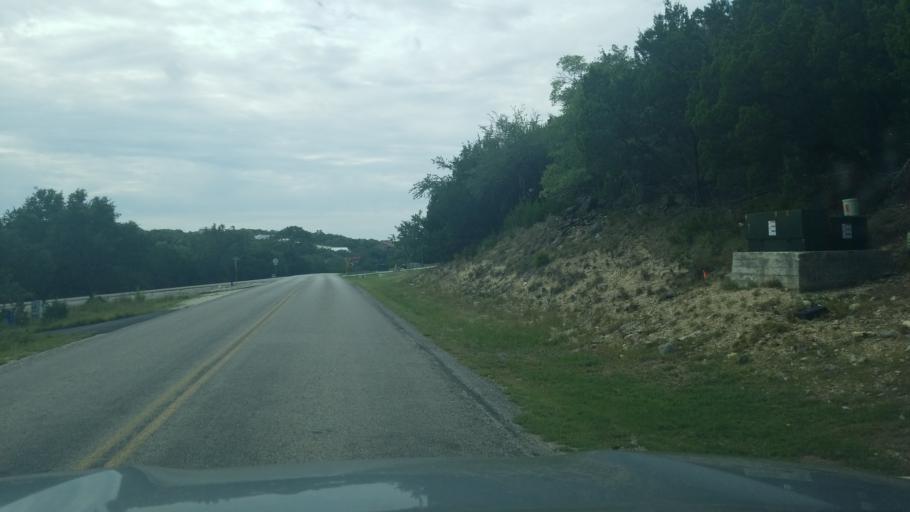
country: US
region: Texas
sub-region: Comal County
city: Bulverde
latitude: 29.8151
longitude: -98.4068
